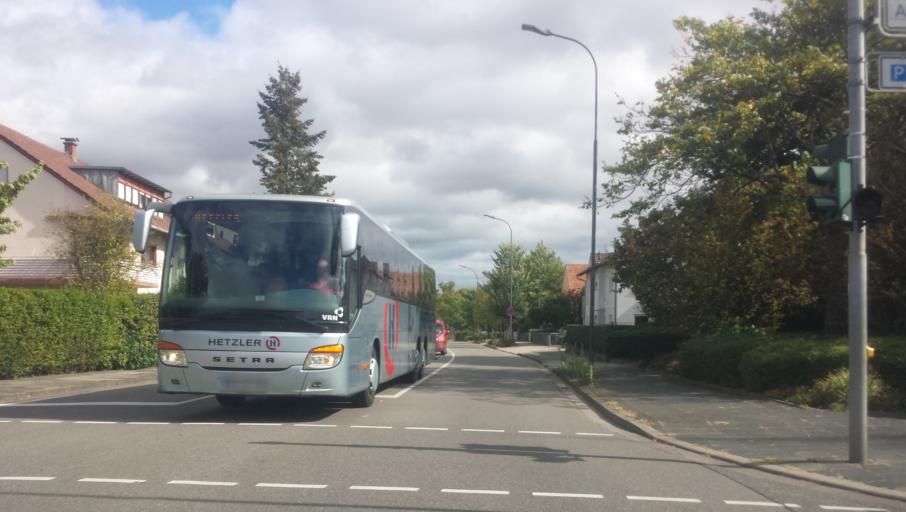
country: DE
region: Rheinland-Pfalz
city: Landau in der Pfalz
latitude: 49.2071
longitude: 8.1101
